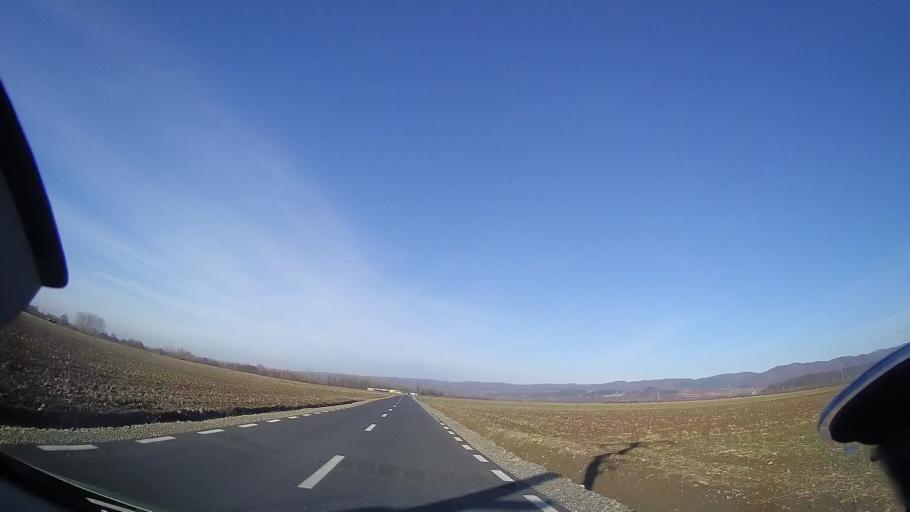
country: RO
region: Bihor
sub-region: Comuna Vadu Crisului
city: Vadu Crisului
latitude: 46.9952
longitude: 22.5070
